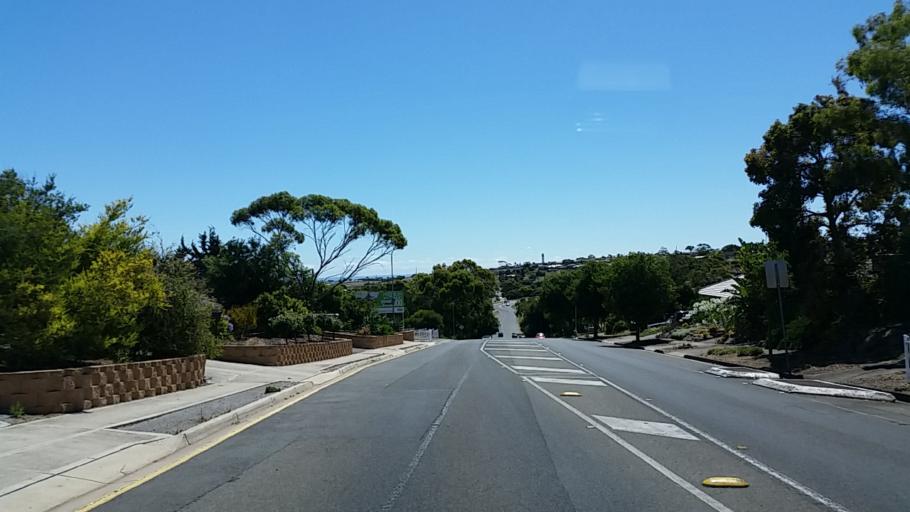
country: AU
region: South Australia
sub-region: Marion
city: Trott Park
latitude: -35.0762
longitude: 138.5374
